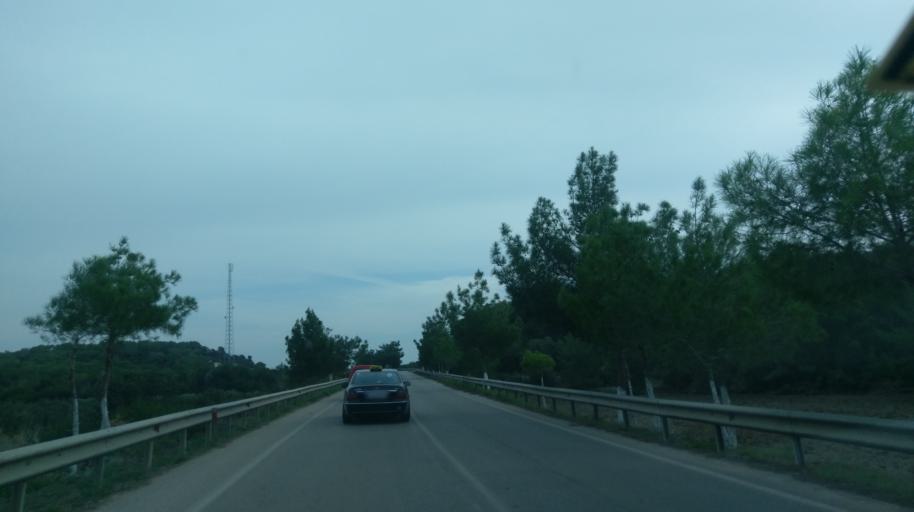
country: CY
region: Ammochostos
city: Leonarisso
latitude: 35.4472
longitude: 34.1341
